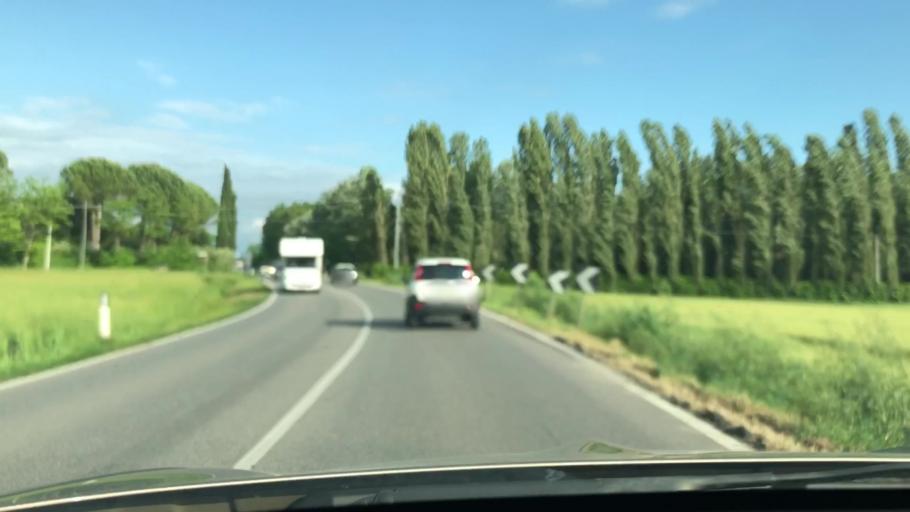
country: IT
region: Tuscany
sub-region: Province of Pisa
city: Treggiaia
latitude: 43.6156
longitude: 10.6781
